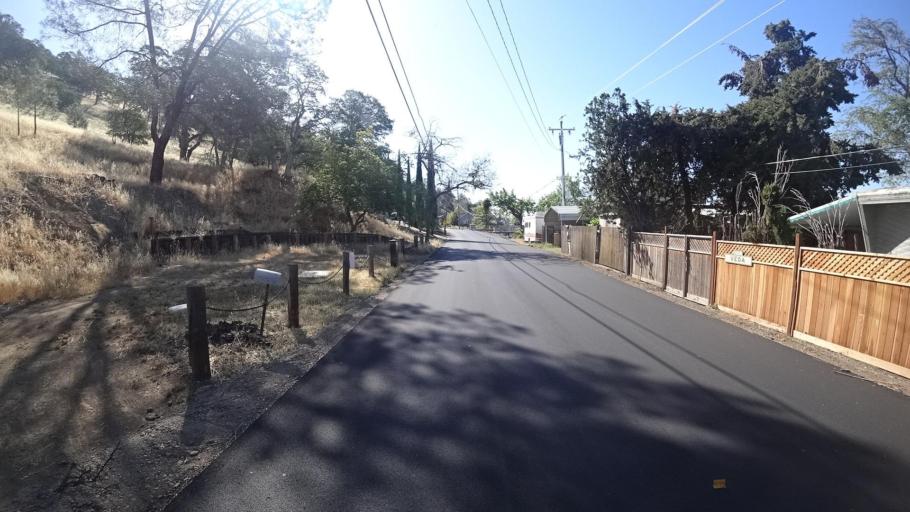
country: US
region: California
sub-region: Lake County
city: Clearlake Oaks
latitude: 38.9751
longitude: -122.6764
